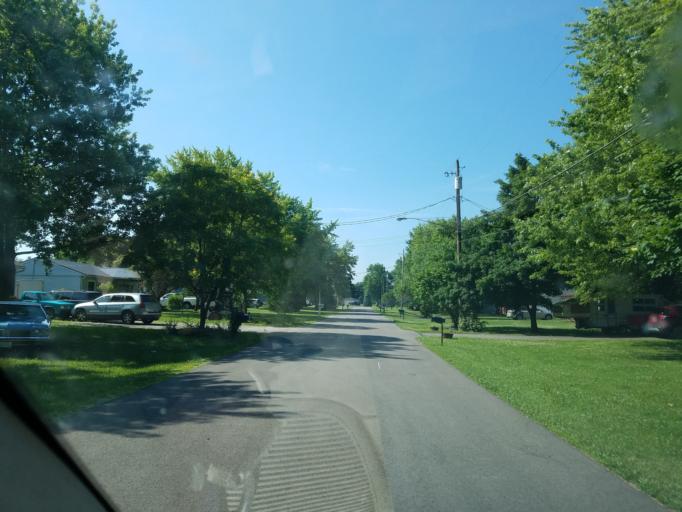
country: US
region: Ohio
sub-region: Marion County
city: Marion
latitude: 40.6470
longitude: -83.0794
